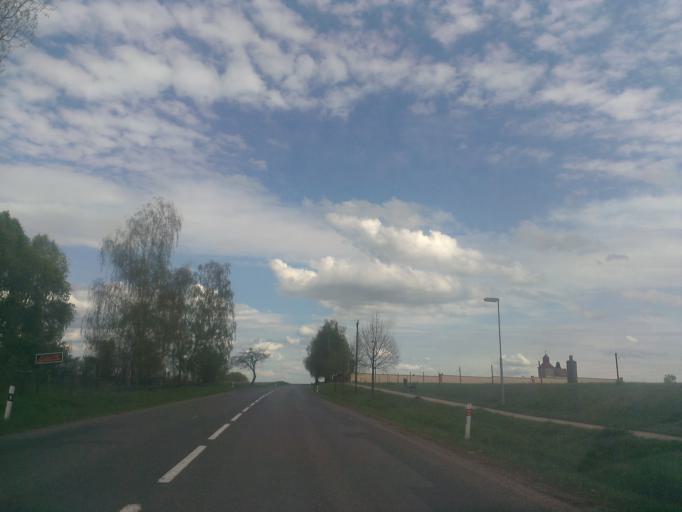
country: CZ
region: South Moravian
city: Dolni Kounice
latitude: 49.1062
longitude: 16.4742
